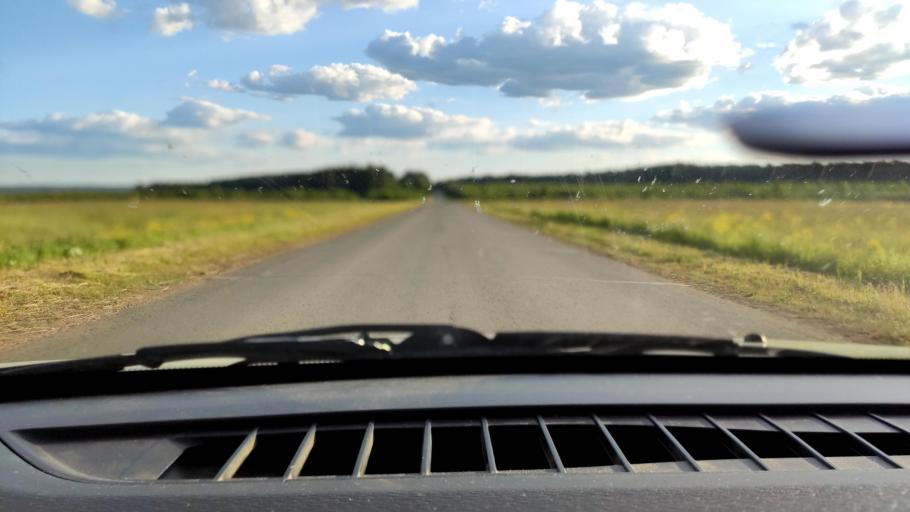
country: RU
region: Perm
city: Uinskoye
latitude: 57.0916
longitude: 56.6336
